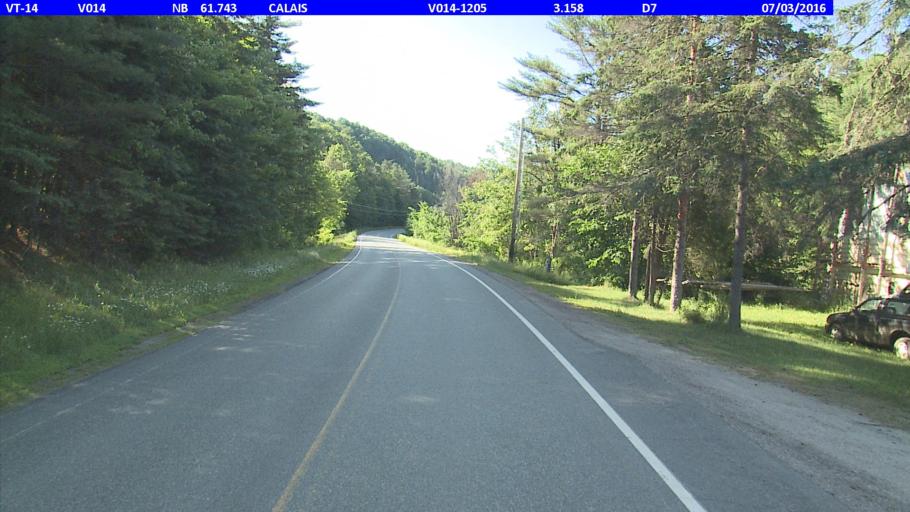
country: US
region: Vermont
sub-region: Washington County
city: Montpelier
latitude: 44.3517
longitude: -72.4427
